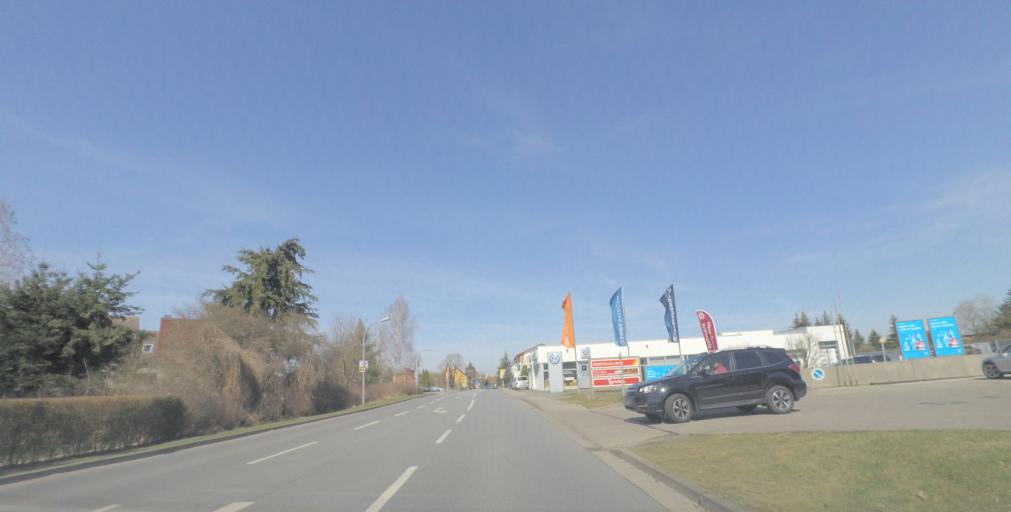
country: DE
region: Brandenburg
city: Neuruppin
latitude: 52.8910
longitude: 12.7980
